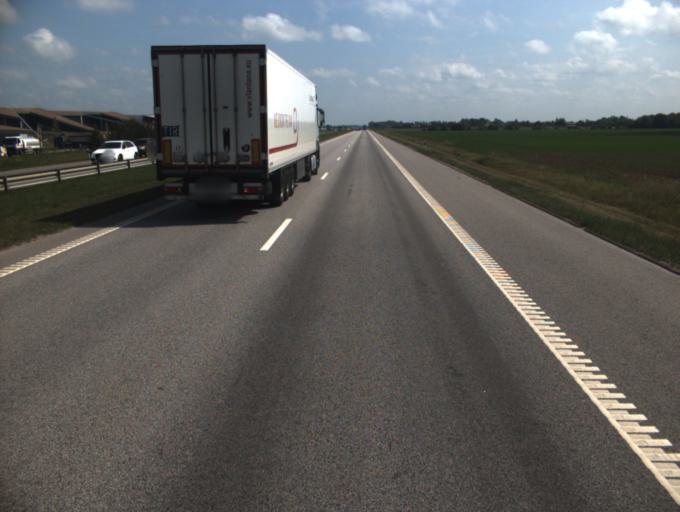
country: LT
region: Klaipedos apskritis
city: Gargzdai
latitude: 55.7133
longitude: 21.2711
